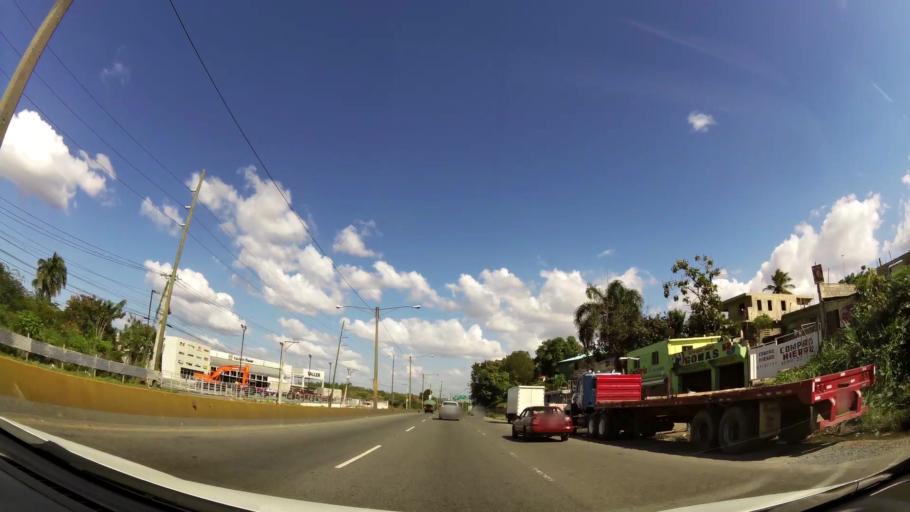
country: DO
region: Santo Domingo
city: Santo Domingo Oeste
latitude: 18.5486
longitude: -70.0448
